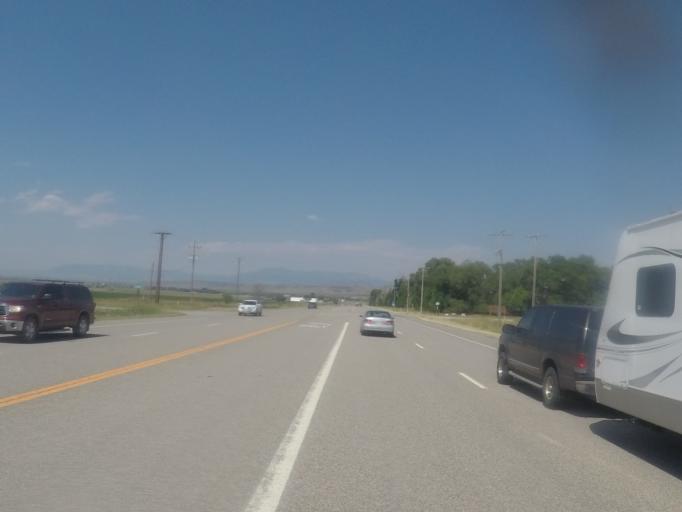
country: US
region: Montana
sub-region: Broadwater County
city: Townsend
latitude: 46.1510
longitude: -111.4672
